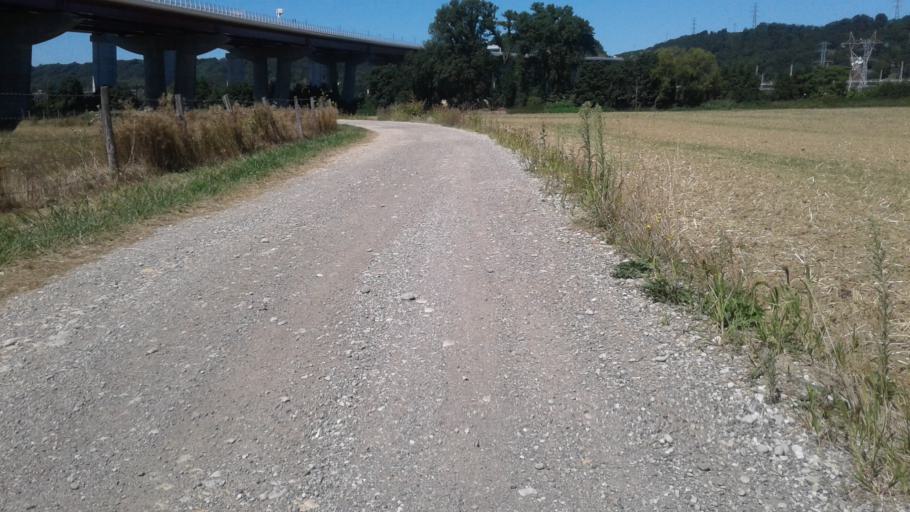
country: FR
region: Rhone-Alpes
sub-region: Departement de l'Ain
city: La Boisse
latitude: 45.8346
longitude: 5.0243
